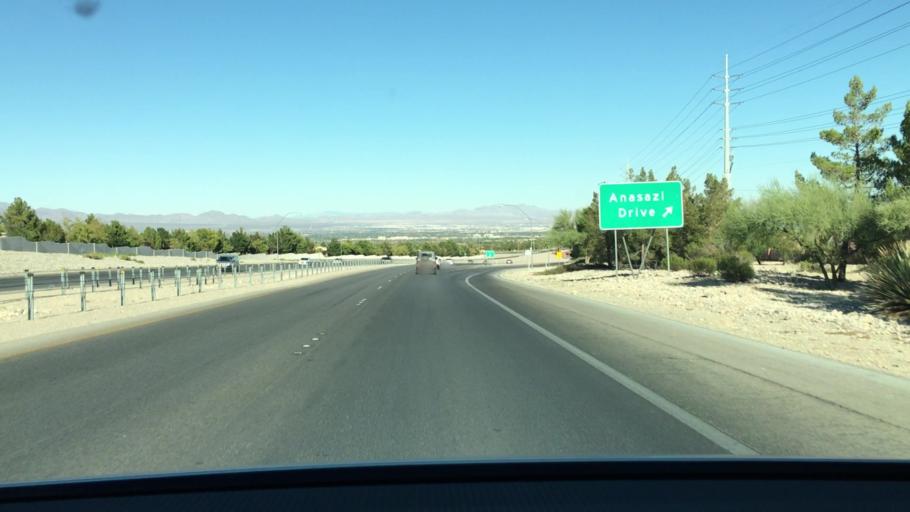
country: US
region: Nevada
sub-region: Clark County
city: Summerlin South
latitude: 36.1931
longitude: -115.3309
